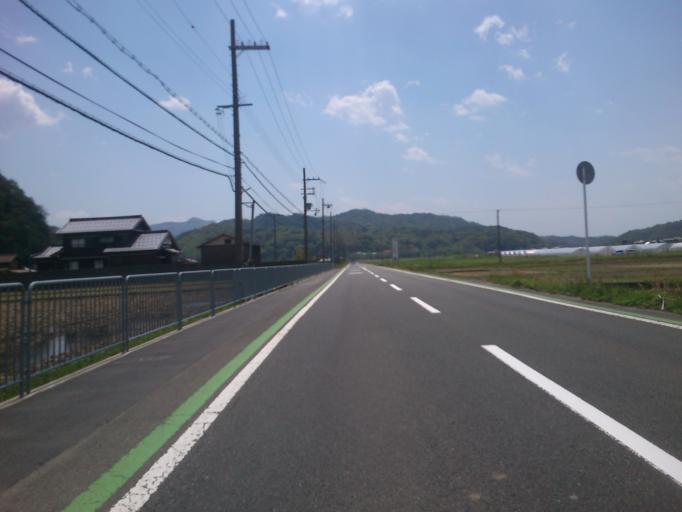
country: JP
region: Kyoto
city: Miyazu
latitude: 35.7234
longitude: 135.1072
